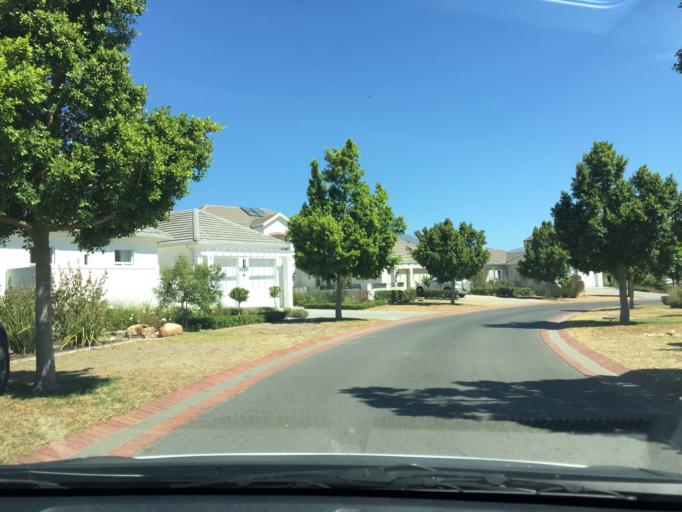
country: ZA
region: Western Cape
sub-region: Cape Winelands District Municipality
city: Paarl
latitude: -33.8040
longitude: 18.9789
